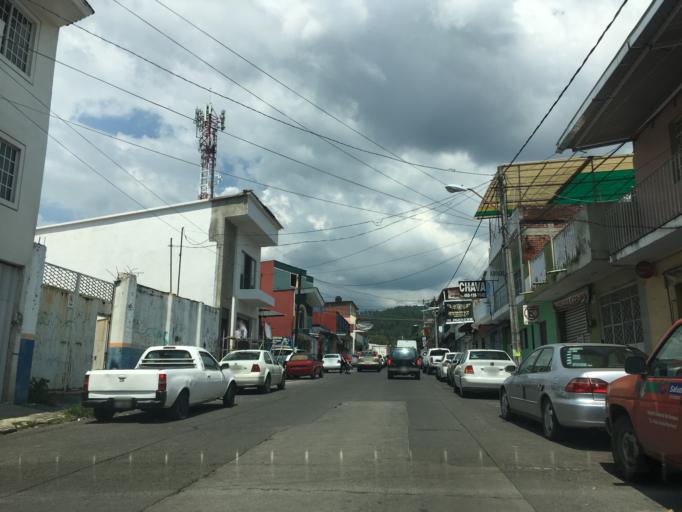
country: MX
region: Michoacan
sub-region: Uruapan
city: Uruapan
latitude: 19.4253
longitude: -102.0548
